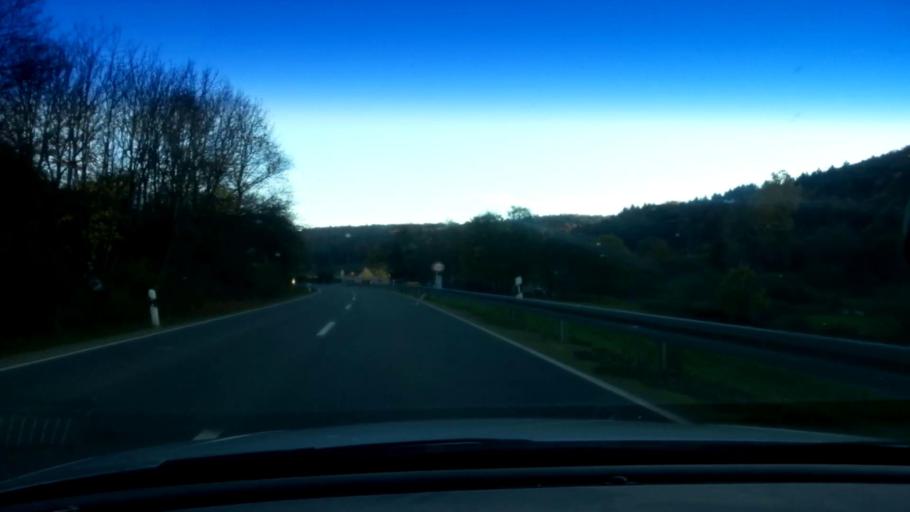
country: DE
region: Bavaria
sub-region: Upper Franconia
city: Heiligenstadt
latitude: 49.8542
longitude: 11.1809
